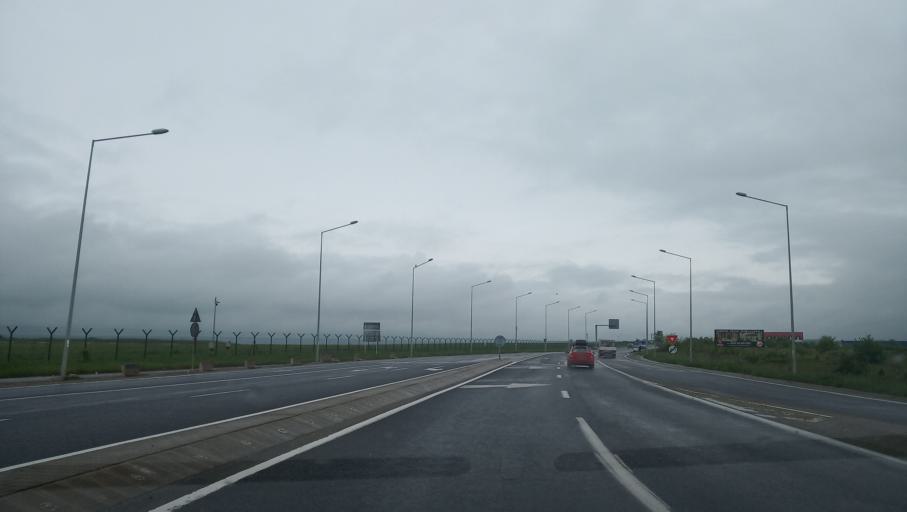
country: RO
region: Sibiu
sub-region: Comuna Cristian
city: Cristian
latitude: 45.7886
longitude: 24.0775
